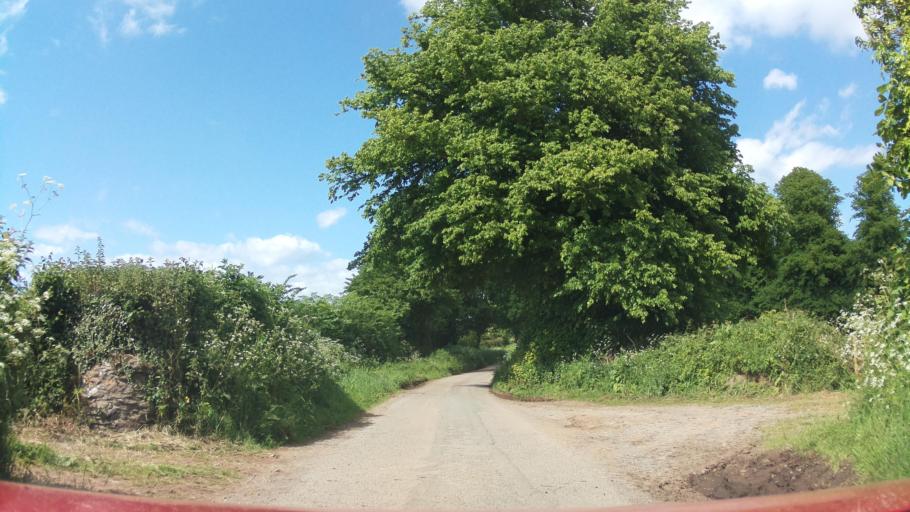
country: GB
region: England
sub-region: Devon
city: Totnes
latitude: 50.4160
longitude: -3.6977
